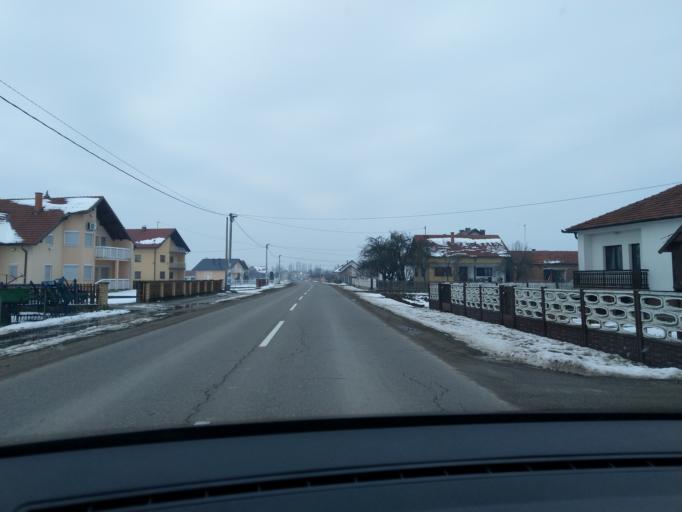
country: BA
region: Republika Srpska
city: Velika Obarska
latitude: 44.7948
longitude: 19.1762
